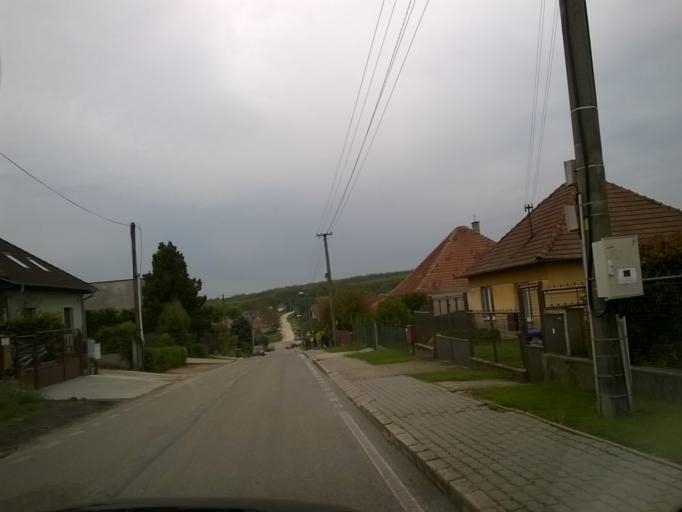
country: SK
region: Nitriansky
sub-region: Okres Nitra
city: Nitra
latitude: 48.2851
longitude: 18.0134
